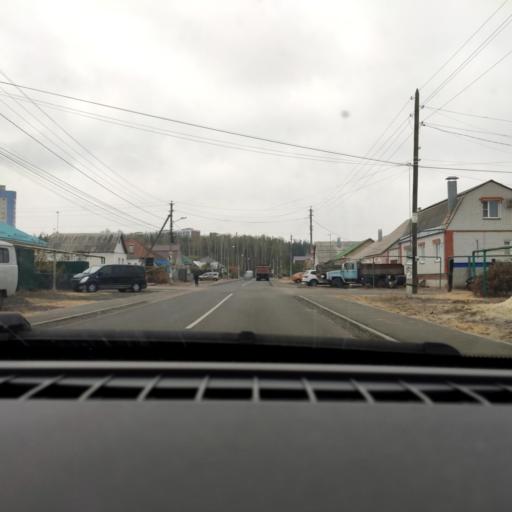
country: RU
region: Voronezj
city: Somovo
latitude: 51.7452
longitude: 39.3244
